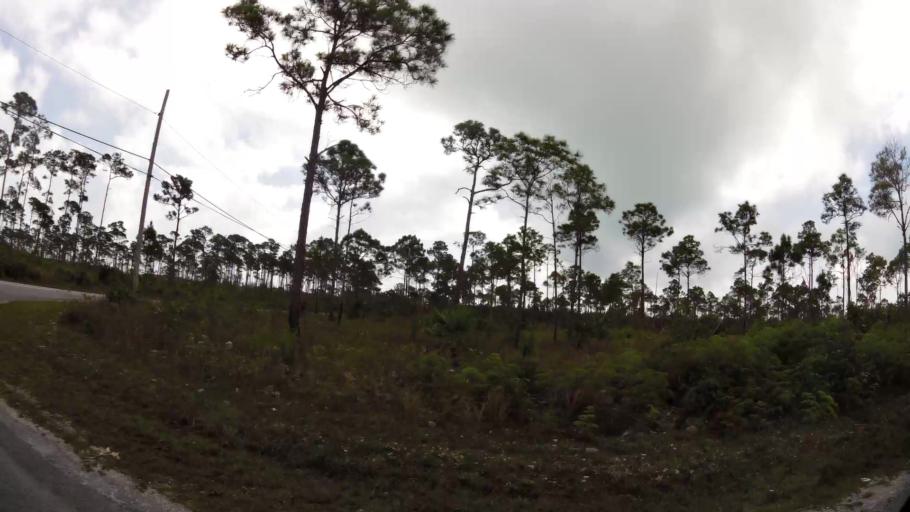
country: BS
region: Freeport
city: Lucaya
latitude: 26.5364
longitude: -78.6013
